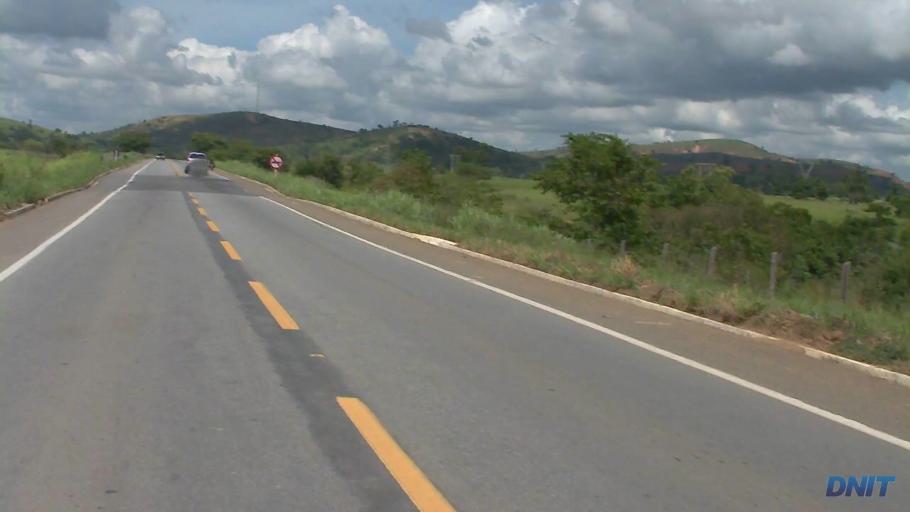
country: BR
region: Minas Gerais
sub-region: Governador Valadares
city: Governador Valadares
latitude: -19.0093
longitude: -42.1359
